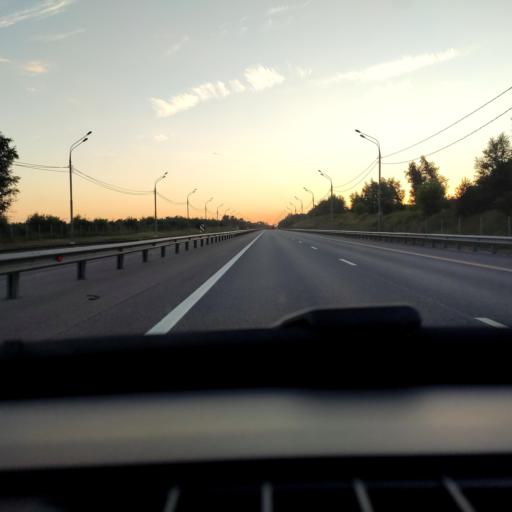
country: RU
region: Lipetsk
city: Zadonsk
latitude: 52.3361
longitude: 38.9821
